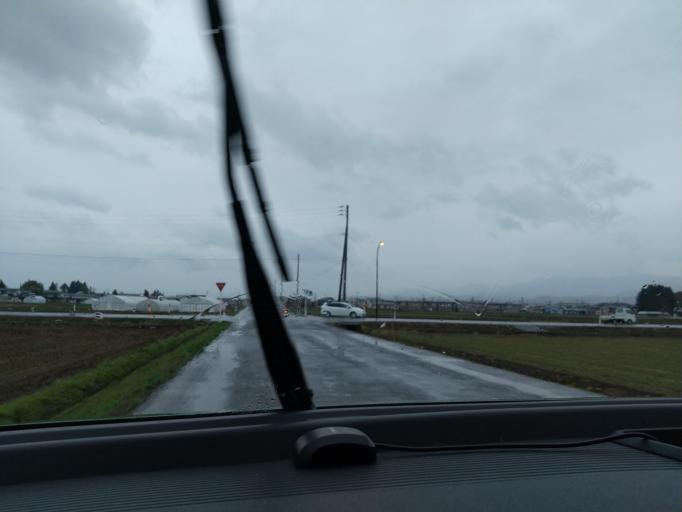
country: JP
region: Akita
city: Yokotemachi
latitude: 39.3154
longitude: 140.5409
